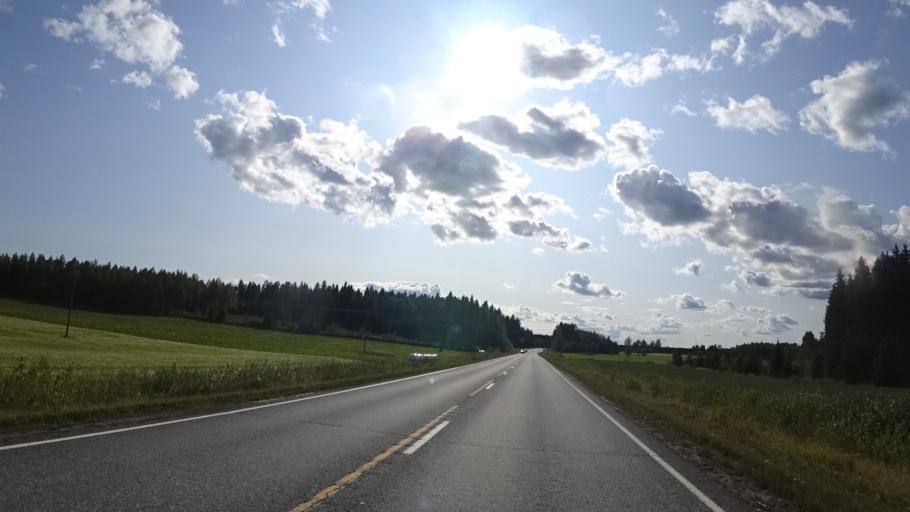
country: FI
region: North Karelia
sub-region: Keski-Karjala
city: Kitee
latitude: 62.0945
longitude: 30.0602
